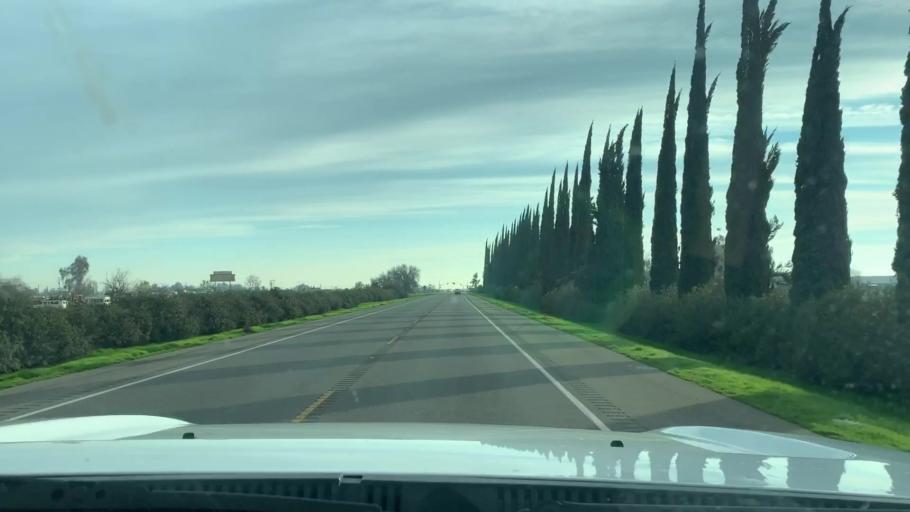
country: US
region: California
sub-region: Fresno County
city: Riverdale
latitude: 36.4369
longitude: -119.8000
